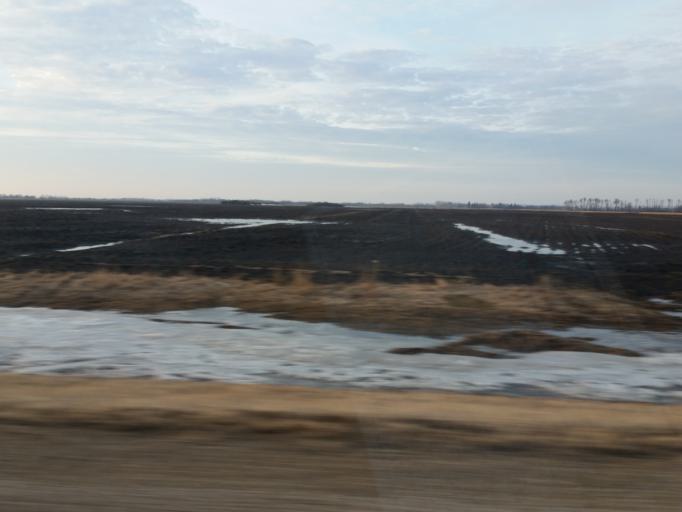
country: US
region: North Dakota
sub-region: Traill County
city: Mayville
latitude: 47.5129
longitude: -97.4342
